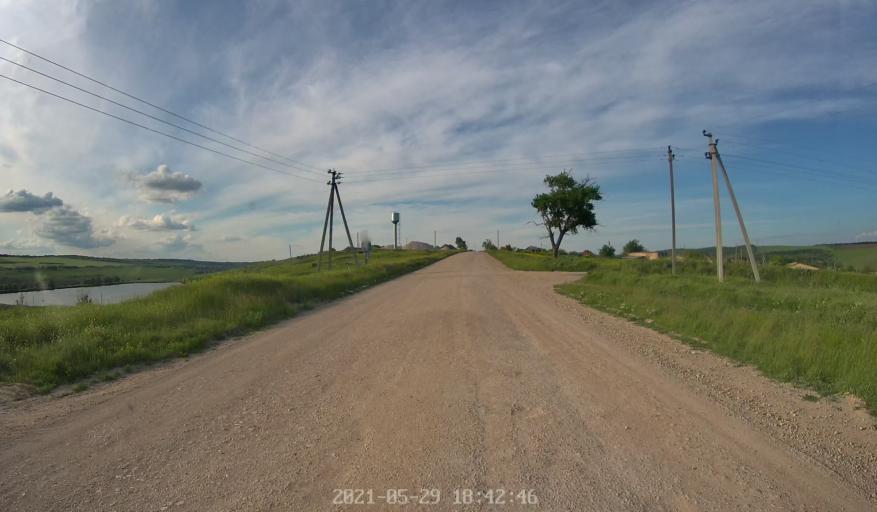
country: MD
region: Chisinau
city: Singera
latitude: 46.8145
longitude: 28.9629
